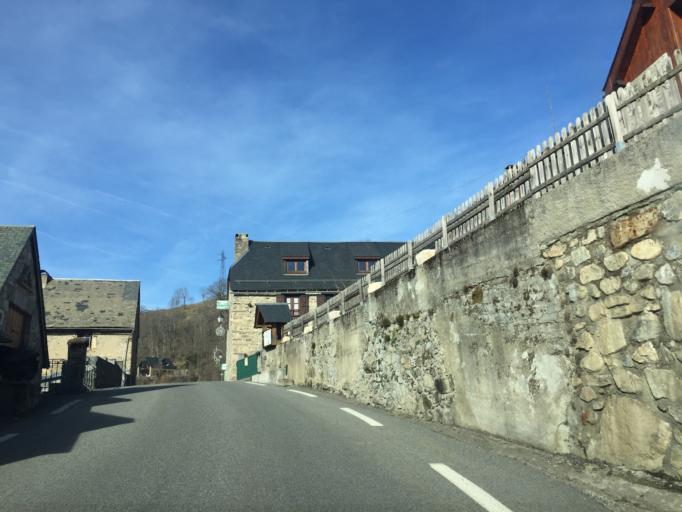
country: FR
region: Midi-Pyrenees
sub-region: Departement des Hautes-Pyrenees
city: Saint-Lary-Soulan
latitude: 42.8050
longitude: 0.4122
